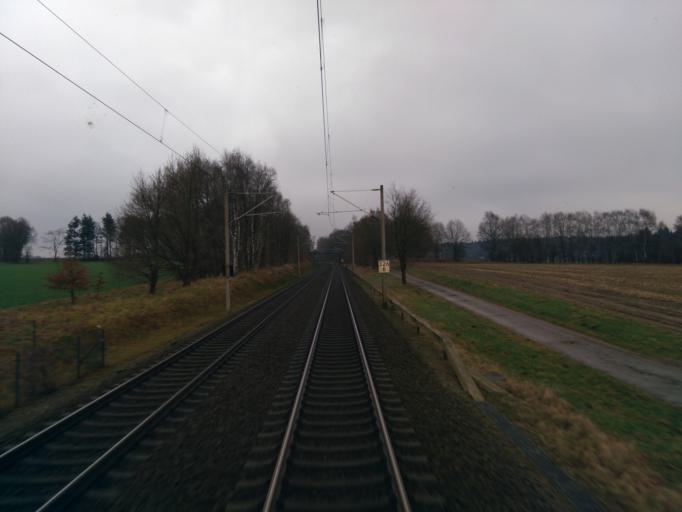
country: DE
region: Lower Saxony
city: Buchholz in der Nordheide
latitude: 53.3464
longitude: 9.9104
